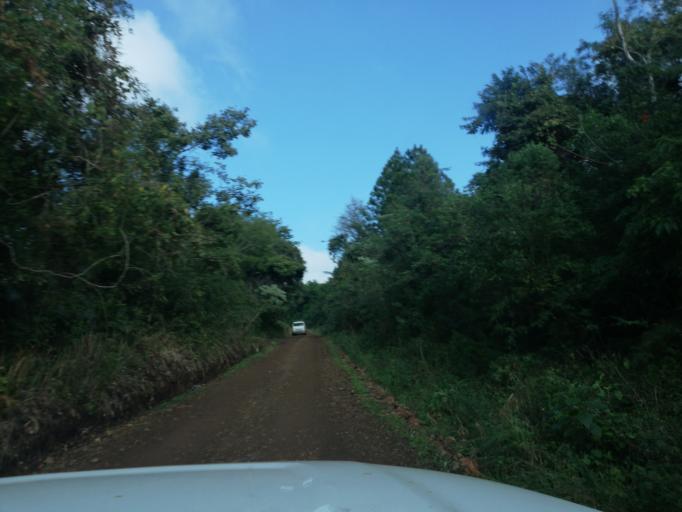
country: AR
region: Misiones
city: Cerro Azul
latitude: -27.5763
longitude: -55.5073
